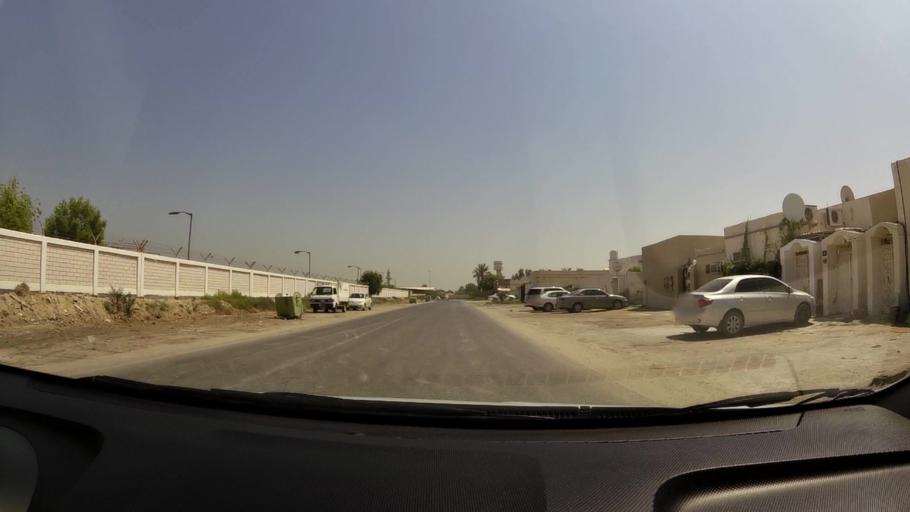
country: AE
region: Umm al Qaywayn
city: Umm al Qaywayn
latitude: 25.5544
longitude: 55.5525
